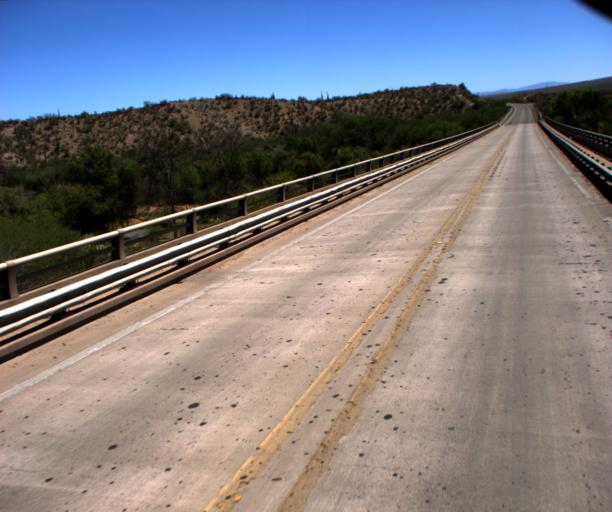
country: US
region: Arizona
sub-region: Pinal County
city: Kearny
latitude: 32.9858
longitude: -110.7697
